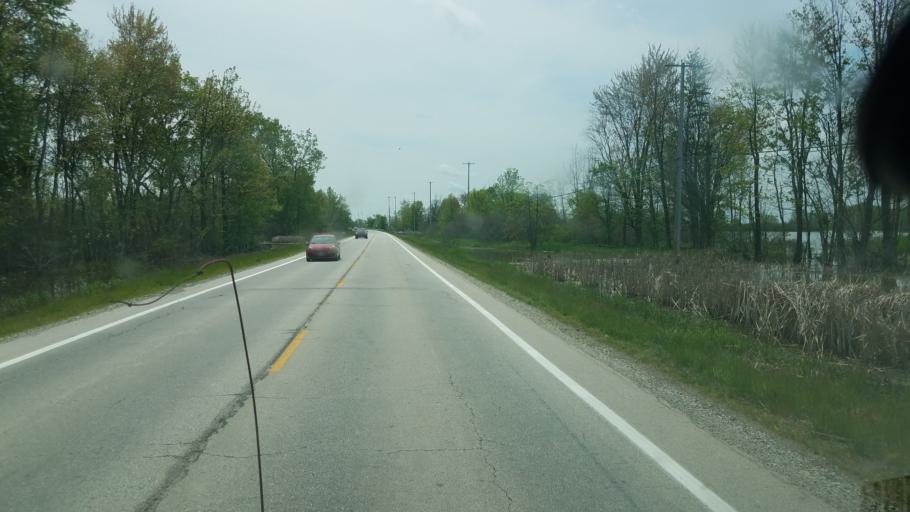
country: US
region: Ohio
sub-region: Ottawa County
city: Oak Harbor
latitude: 41.4561
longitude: -83.0526
